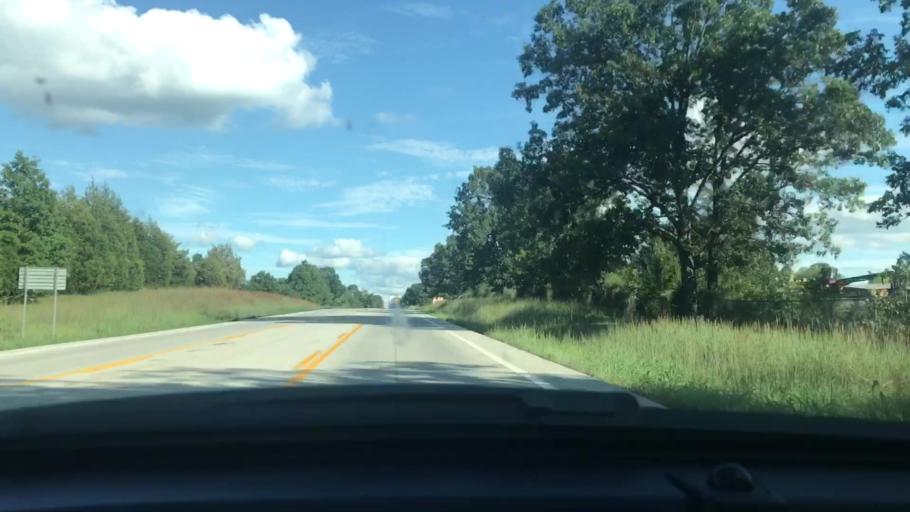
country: US
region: Missouri
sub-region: Howell County
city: West Plains
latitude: 36.6542
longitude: -91.6955
